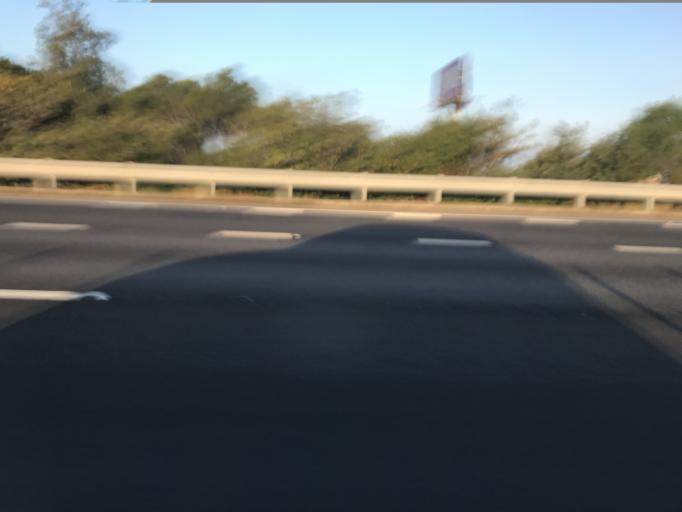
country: TW
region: Taiwan
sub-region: Miaoli
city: Miaoli
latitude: 24.6310
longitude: 120.8150
